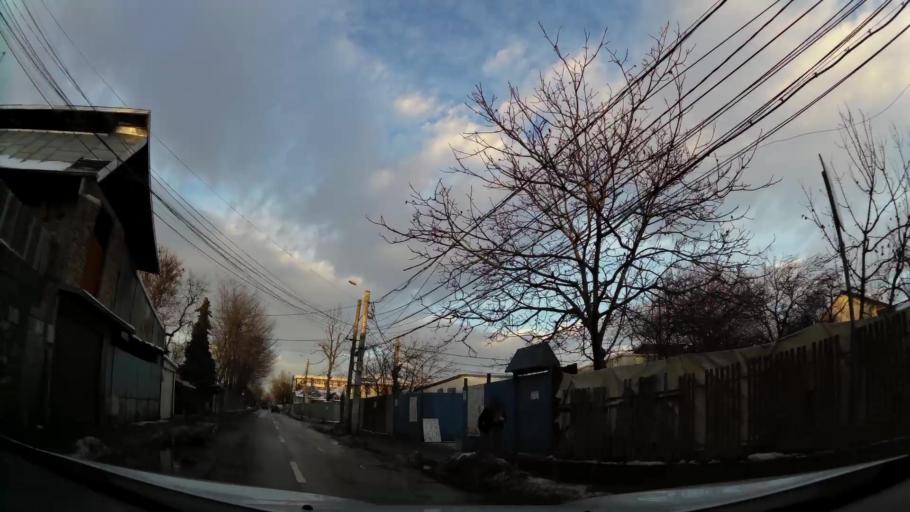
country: RO
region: Ilfov
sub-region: Comuna Popesti-Leordeni
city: Popesti-Leordeni
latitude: 44.3788
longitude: 26.1412
